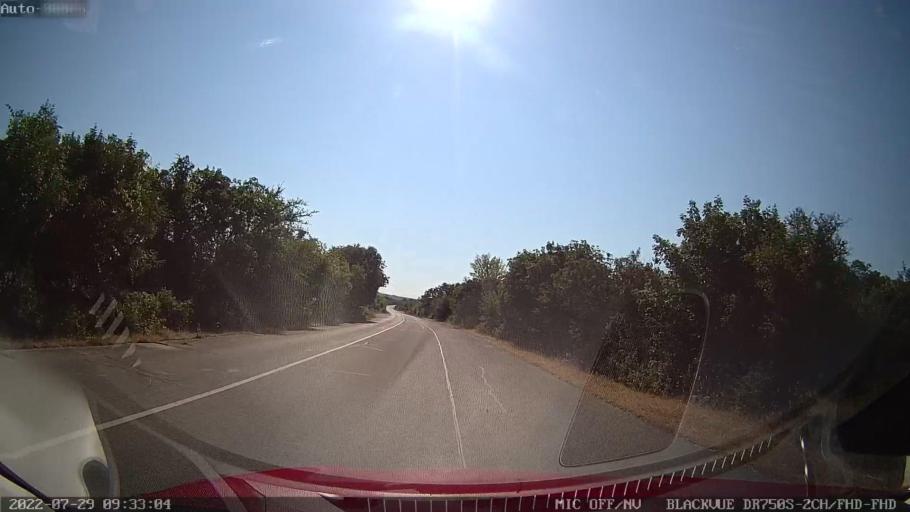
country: HR
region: Zadarska
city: Obrovac
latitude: 44.1796
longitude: 15.7212
